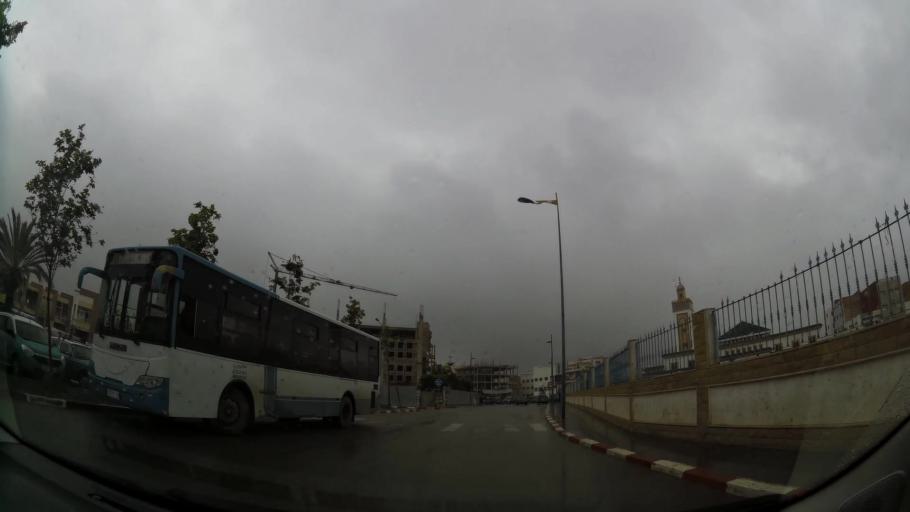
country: MA
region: Taza-Al Hoceima-Taounate
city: Imzourene
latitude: 35.1493
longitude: -3.8477
